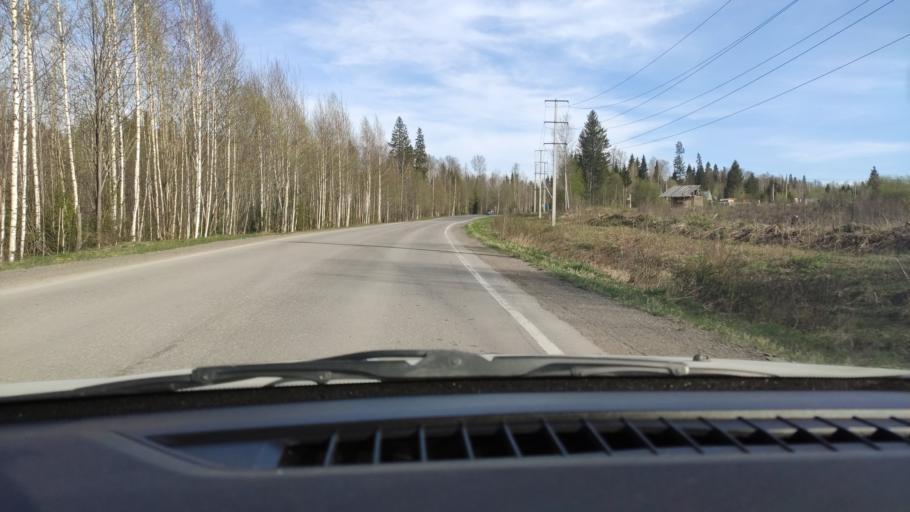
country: RU
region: Perm
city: Novyye Lyady
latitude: 57.9566
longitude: 56.5642
